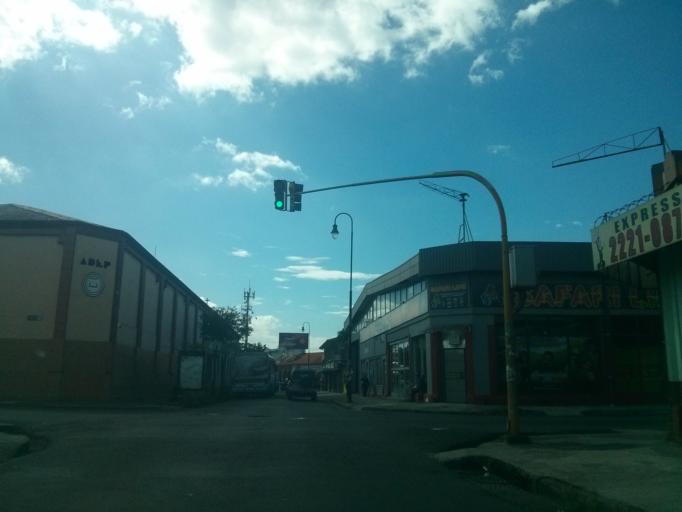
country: CR
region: San Jose
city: San Jose
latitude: 9.9291
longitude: -84.0834
